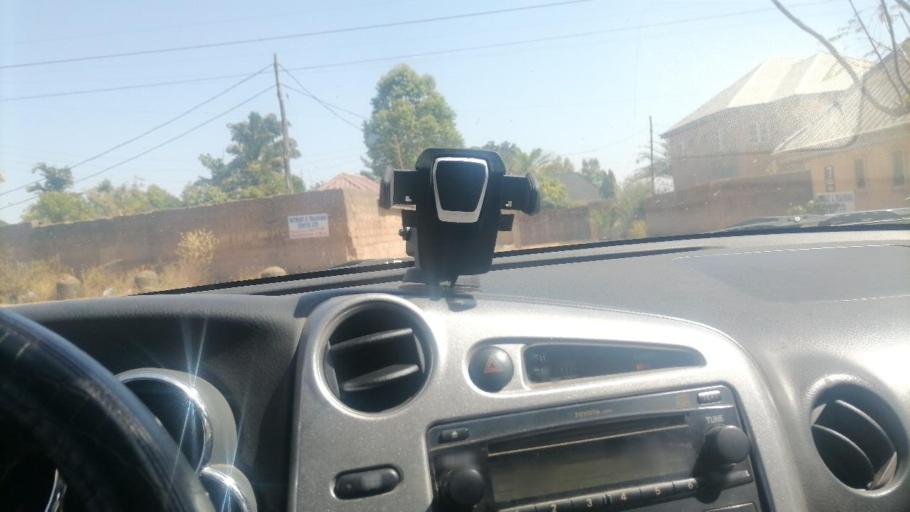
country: NG
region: Plateau
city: Jos
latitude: 9.8677
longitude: 8.9072
